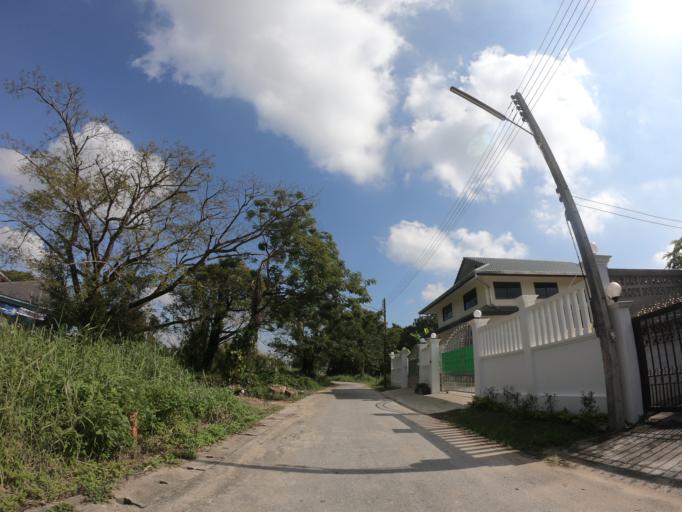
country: TH
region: Chiang Mai
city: Chiang Mai
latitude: 18.7884
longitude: 99.0366
